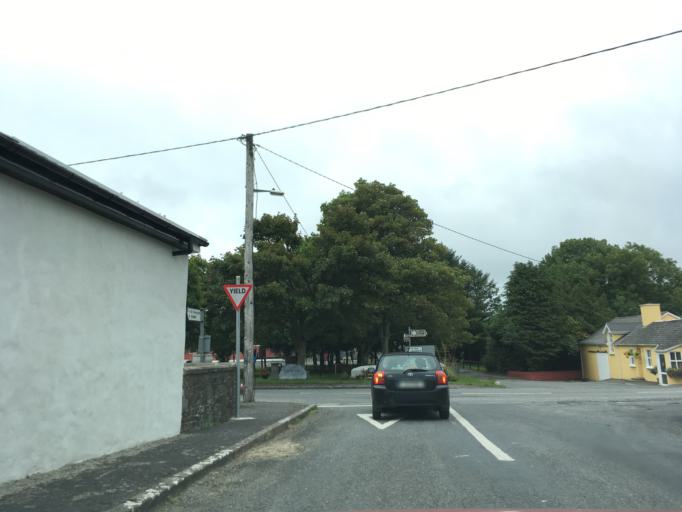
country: IE
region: Munster
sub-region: An Clar
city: Ennis
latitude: 52.7182
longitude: -9.0683
